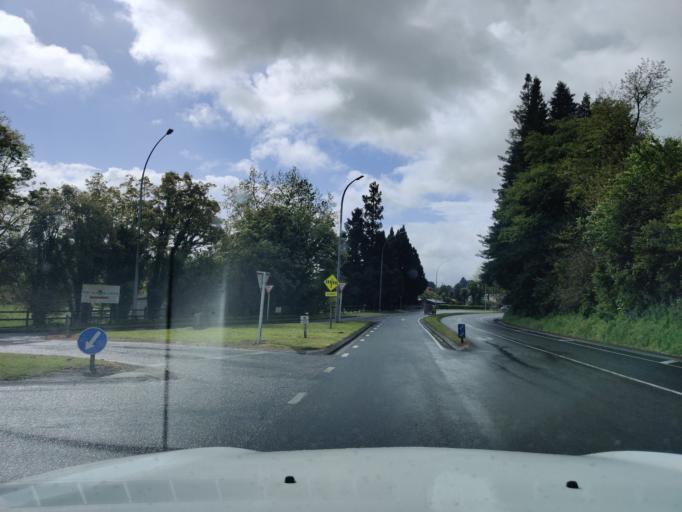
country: NZ
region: Waikato
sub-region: Matamata-Piako District
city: Matamata
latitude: -37.9756
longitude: 175.7539
